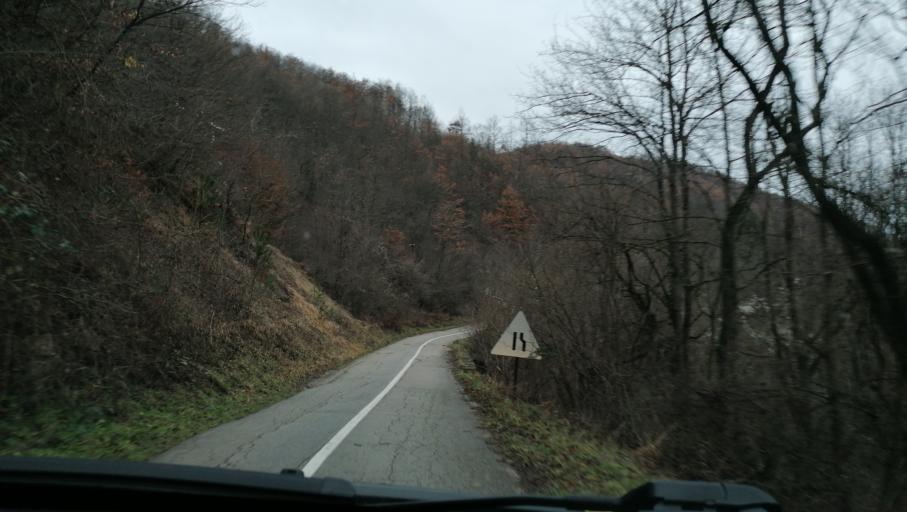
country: RS
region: Central Serbia
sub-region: Pirotski Okrug
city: Dimitrovgrad
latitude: 42.9761
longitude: 22.7848
